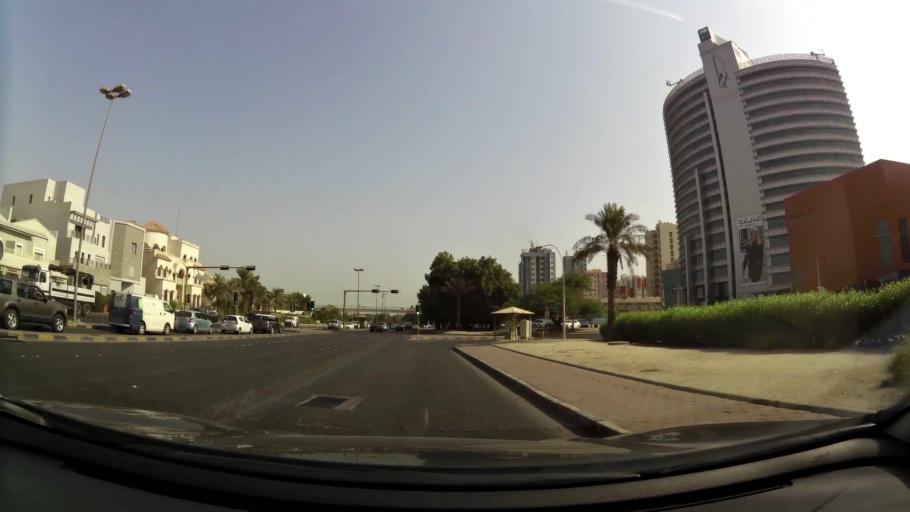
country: KW
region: Al Asimah
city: Ad Dasmah
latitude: 29.3469
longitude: 48.0104
